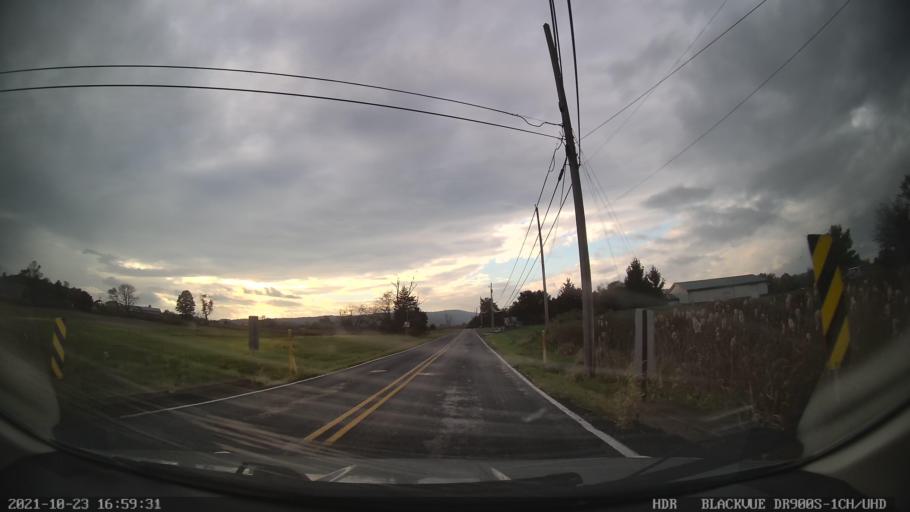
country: US
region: Pennsylvania
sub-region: Montgomery County
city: East Greenville
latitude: 40.4286
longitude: -75.5449
